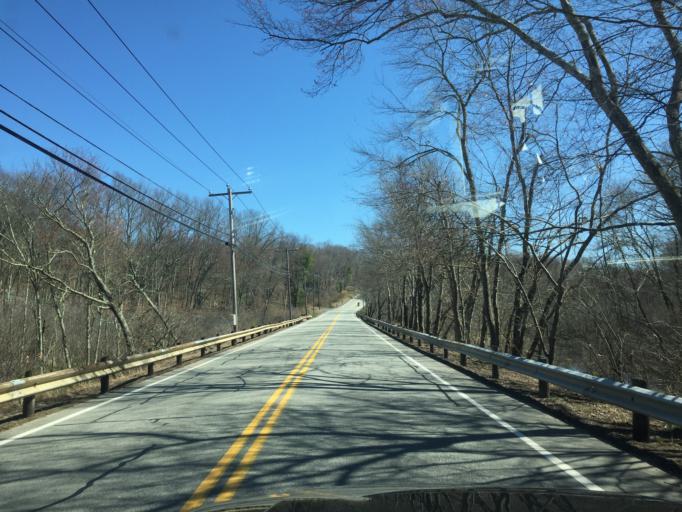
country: US
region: Connecticut
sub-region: Hartford County
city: Terramuggus
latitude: 41.6455
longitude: -72.4787
